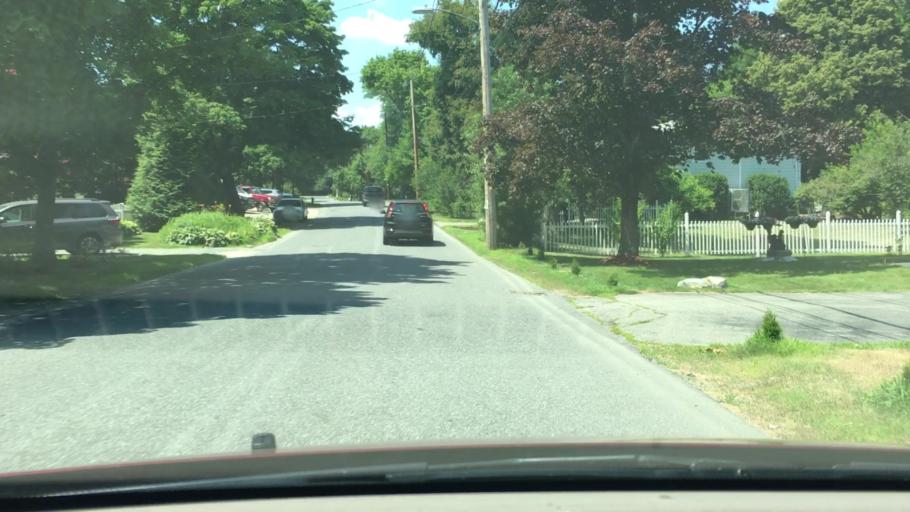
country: US
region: Massachusetts
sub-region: Middlesex County
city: Lexington
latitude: 42.4338
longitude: -71.1920
